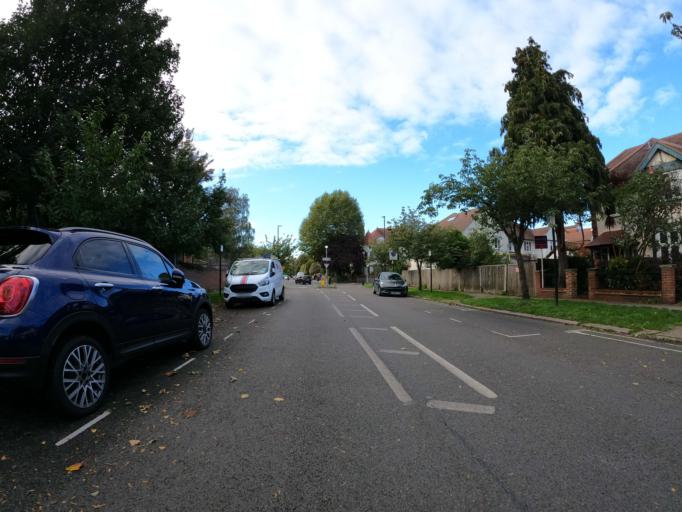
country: GB
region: England
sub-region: Greater London
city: Acton
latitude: 51.4846
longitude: -0.2684
